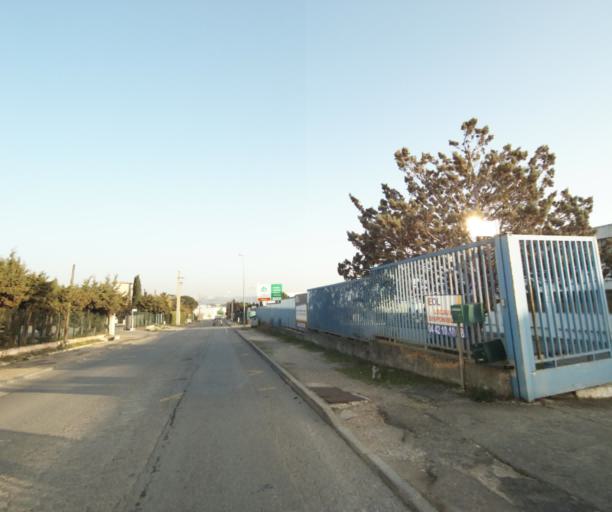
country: FR
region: Provence-Alpes-Cote d'Azur
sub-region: Departement des Bouches-du-Rhone
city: Vitrolles
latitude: 43.4375
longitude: 5.2478
